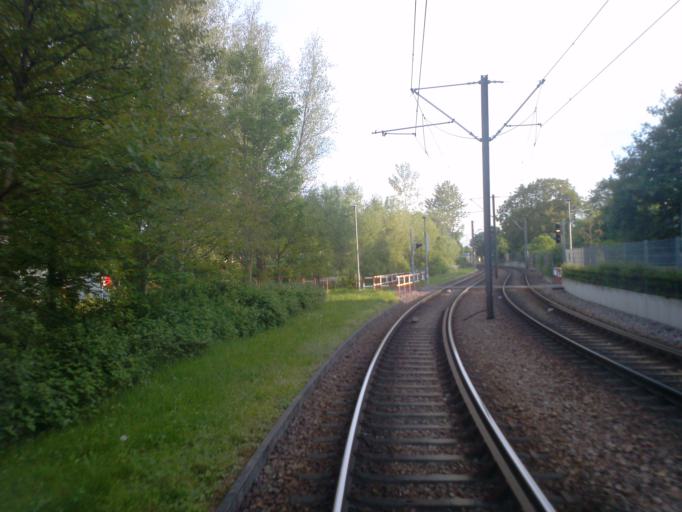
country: DE
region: Baden-Wuerttemberg
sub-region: Karlsruhe Region
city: Weingarten
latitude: 49.0706
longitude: 8.4754
